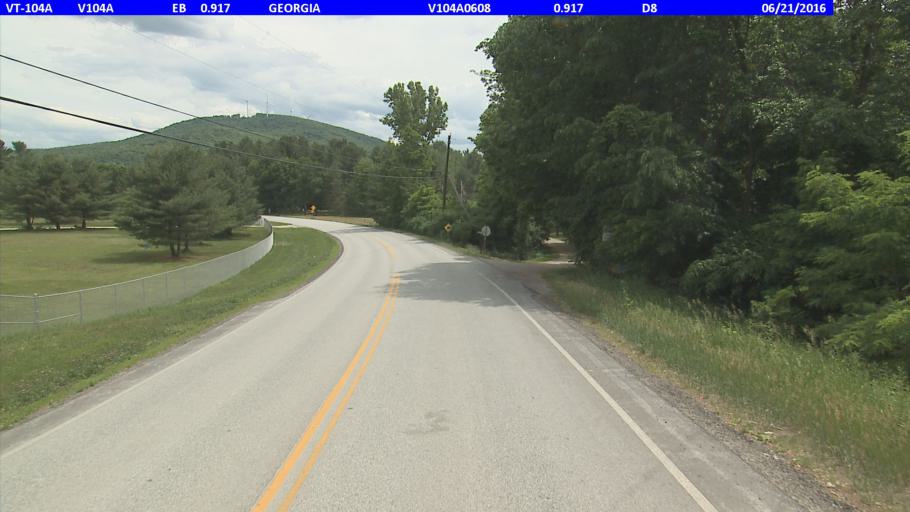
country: US
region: Vermont
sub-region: Chittenden County
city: Milton
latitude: 44.6851
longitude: -73.0962
